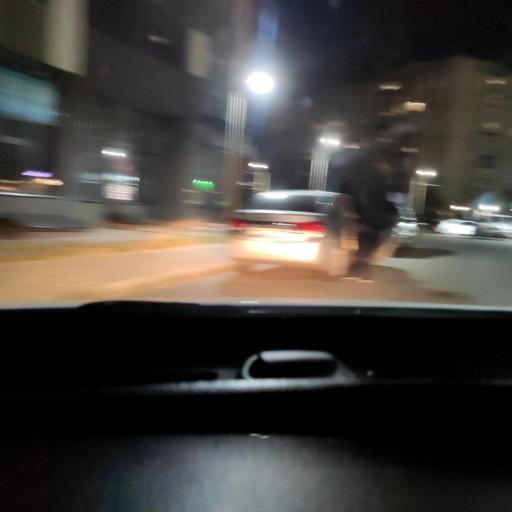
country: RU
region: Voronezj
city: Maslovka
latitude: 51.5887
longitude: 39.2432
